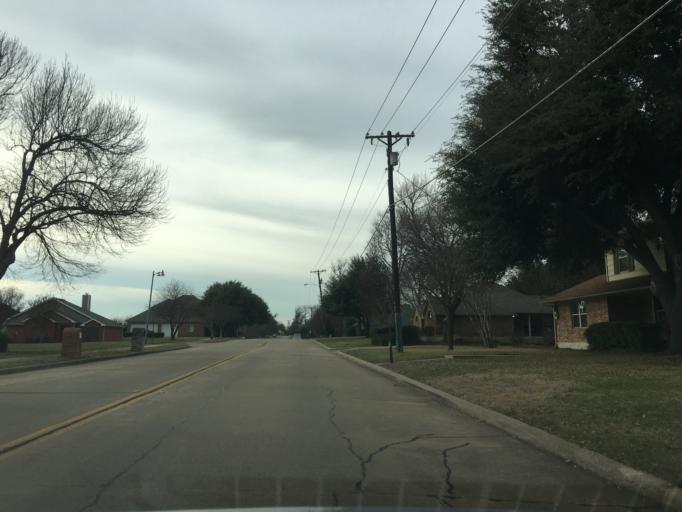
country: US
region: Texas
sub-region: Collin County
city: McKinney
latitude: 33.1949
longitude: -96.6456
